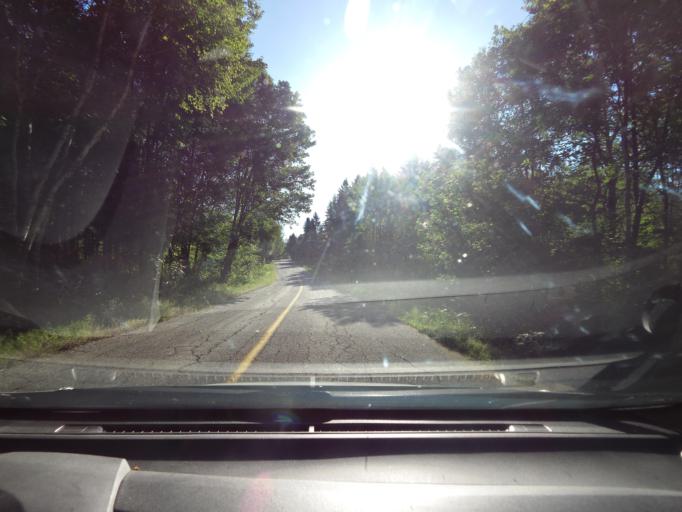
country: CA
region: Quebec
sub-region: Mauricie
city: Becancour
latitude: 46.5518
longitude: -72.3806
